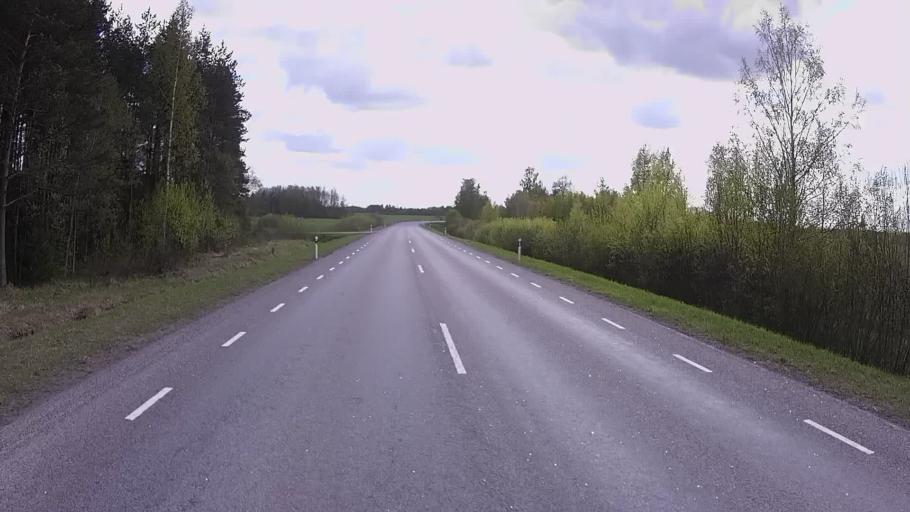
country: EE
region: Tartu
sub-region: Alatskivi vald
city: Kallaste
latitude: 58.5196
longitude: 27.0023
